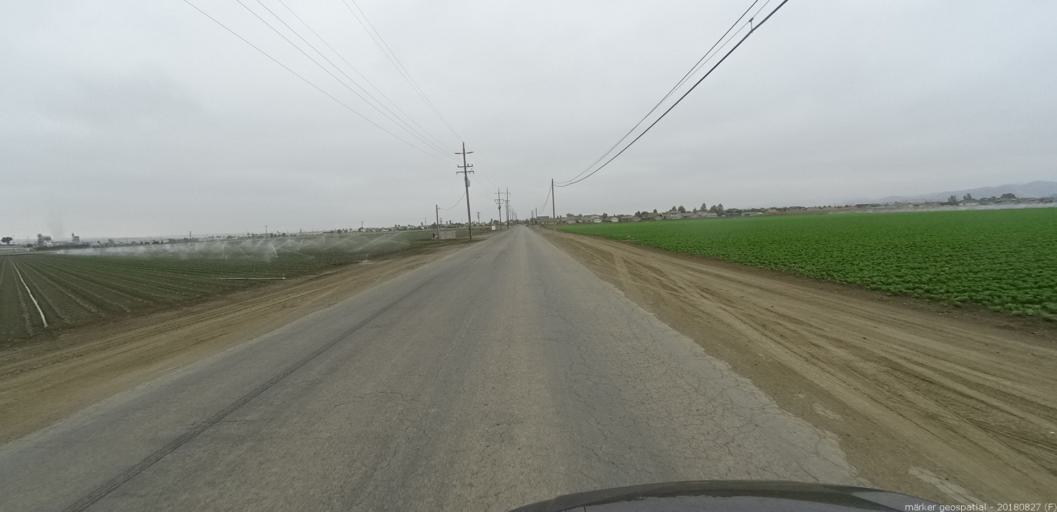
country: US
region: California
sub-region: Monterey County
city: King City
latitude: 36.2268
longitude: -121.1383
